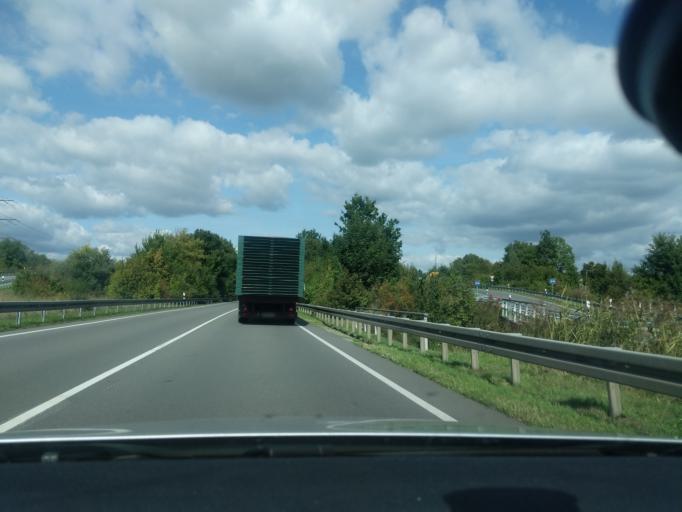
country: DE
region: Lower Saxony
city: Bohmte
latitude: 52.3659
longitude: 8.2995
